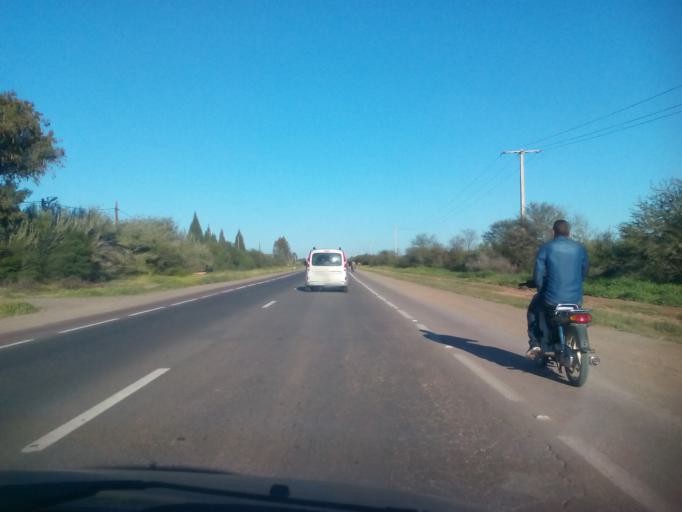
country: MA
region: Marrakech-Tensift-Al Haouz
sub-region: Marrakech
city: Marrakesh
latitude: 31.6303
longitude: -8.1586
